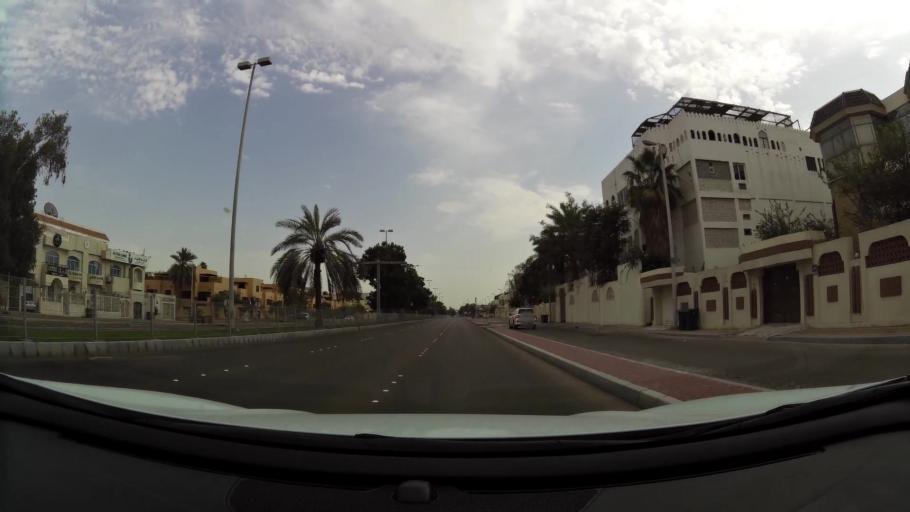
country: AE
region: Abu Dhabi
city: Abu Dhabi
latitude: 24.4619
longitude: 54.3696
